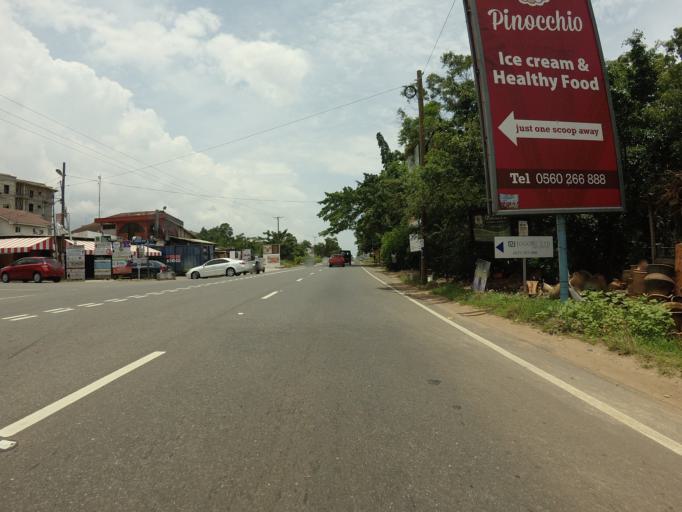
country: GH
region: Greater Accra
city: Medina Estates
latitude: 5.6334
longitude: -0.1493
